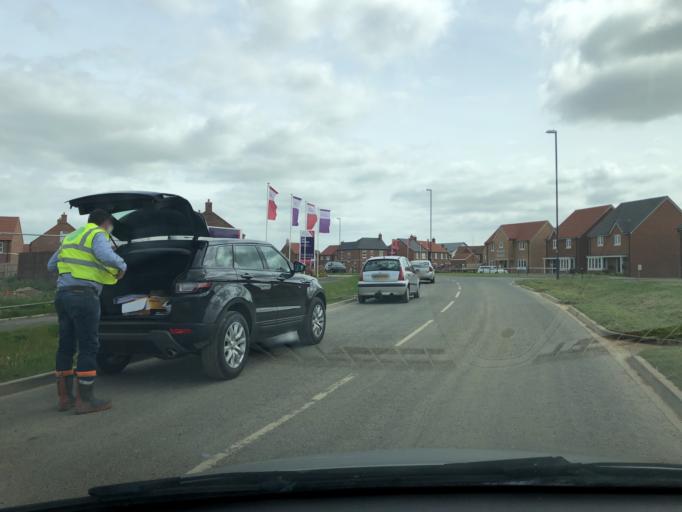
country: GB
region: England
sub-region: North Yorkshire
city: Thirsk
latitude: 54.2214
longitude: -1.3544
